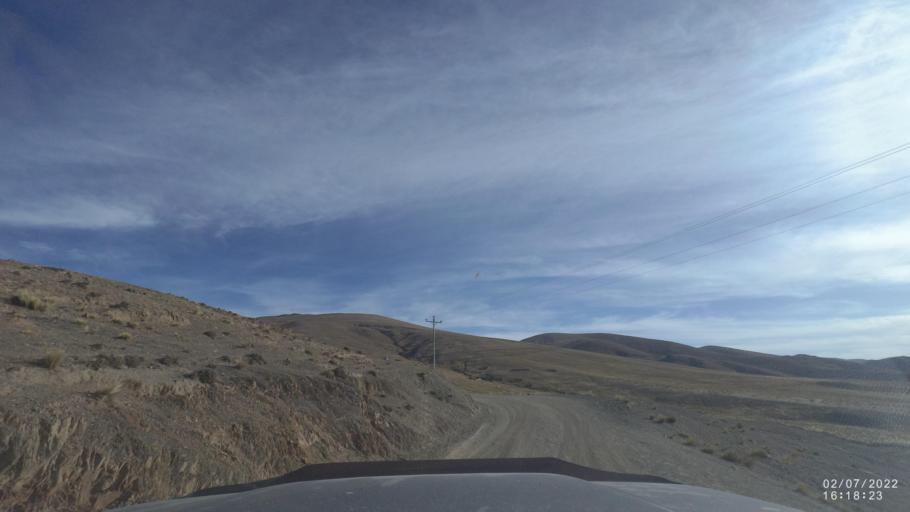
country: BO
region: Cochabamba
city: Irpa Irpa
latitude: -17.9267
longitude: -66.4421
